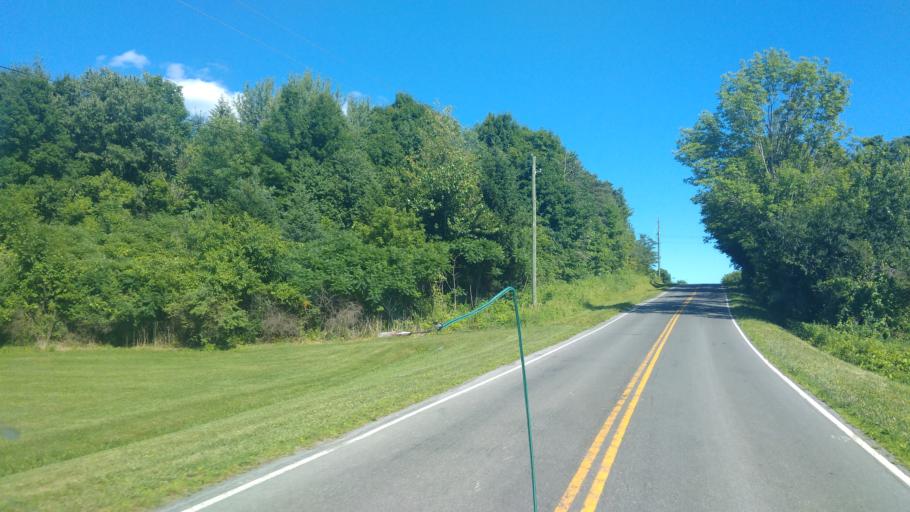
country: US
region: New York
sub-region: Wayne County
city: Clyde
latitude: 43.0256
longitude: -76.8282
